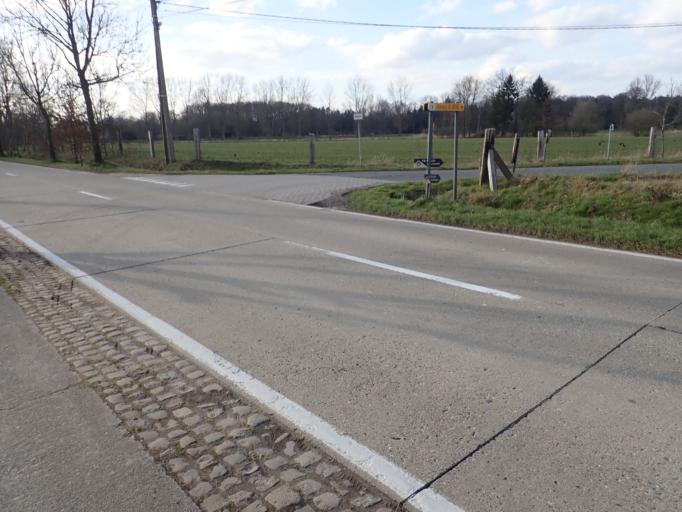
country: BE
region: Flanders
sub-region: Provincie Antwerpen
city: Zandhoven
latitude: 51.1917
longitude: 4.6729
